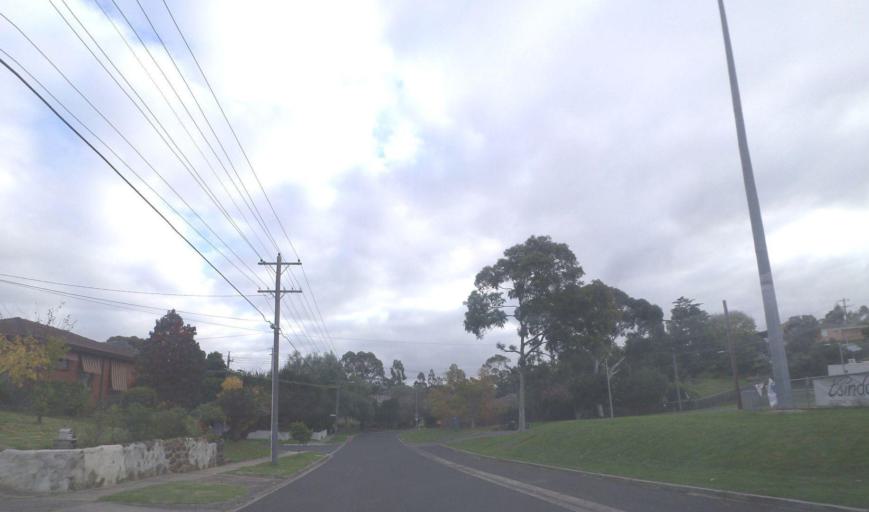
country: AU
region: Victoria
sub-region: Whitehorse
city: Mont Albert North
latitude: -37.7923
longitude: 145.1099
